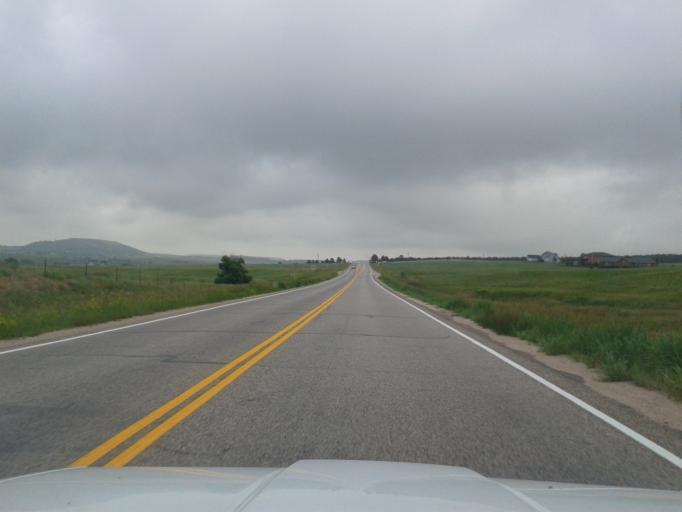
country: US
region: Colorado
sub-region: El Paso County
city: Woodmoor
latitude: 39.1237
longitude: -104.7665
